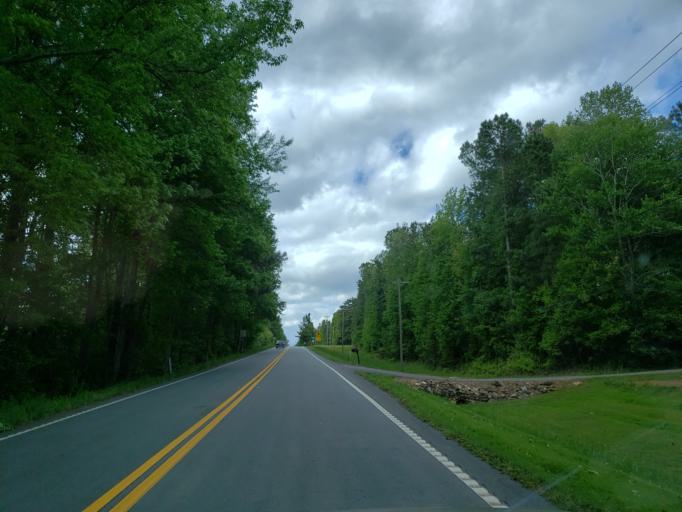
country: US
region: Georgia
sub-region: Carroll County
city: Mount Zion
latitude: 33.6569
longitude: -85.2689
